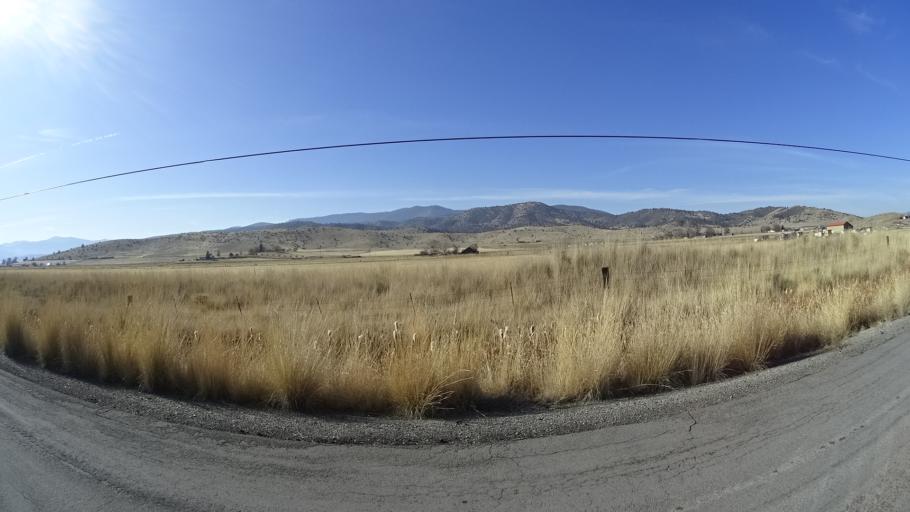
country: US
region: California
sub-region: Siskiyou County
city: Montague
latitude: 41.6104
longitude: -122.5231
